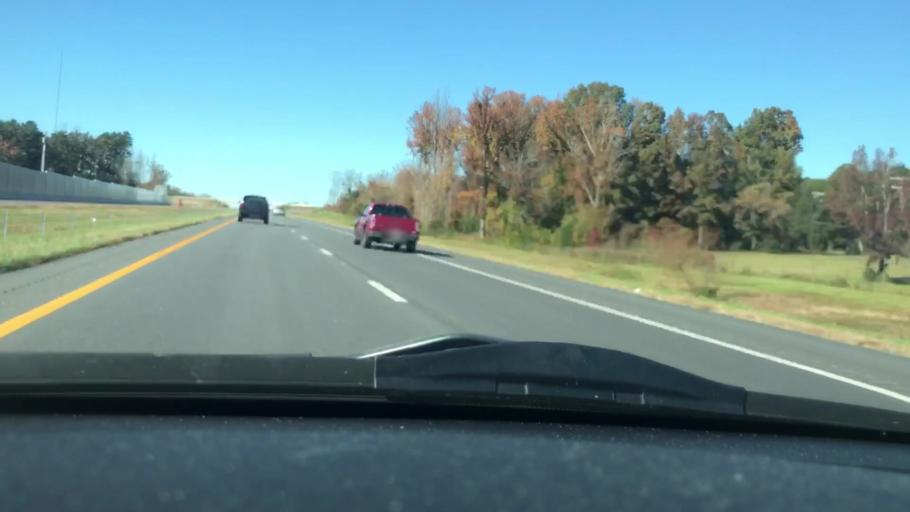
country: US
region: North Carolina
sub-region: Guilford County
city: Summerfield
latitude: 36.2605
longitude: -79.9263
